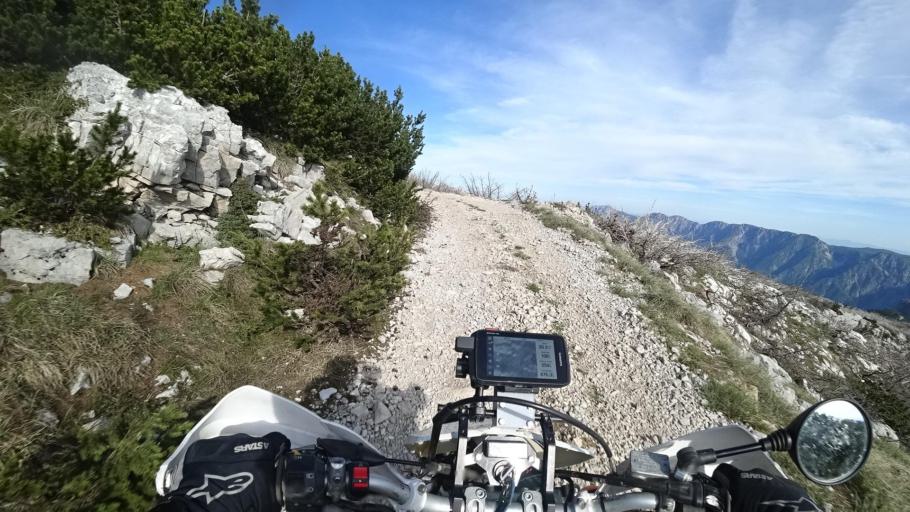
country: BA
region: Federation of Bosnia and Herzegovina
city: Kocerin
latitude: 43.5874
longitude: 17.5345
